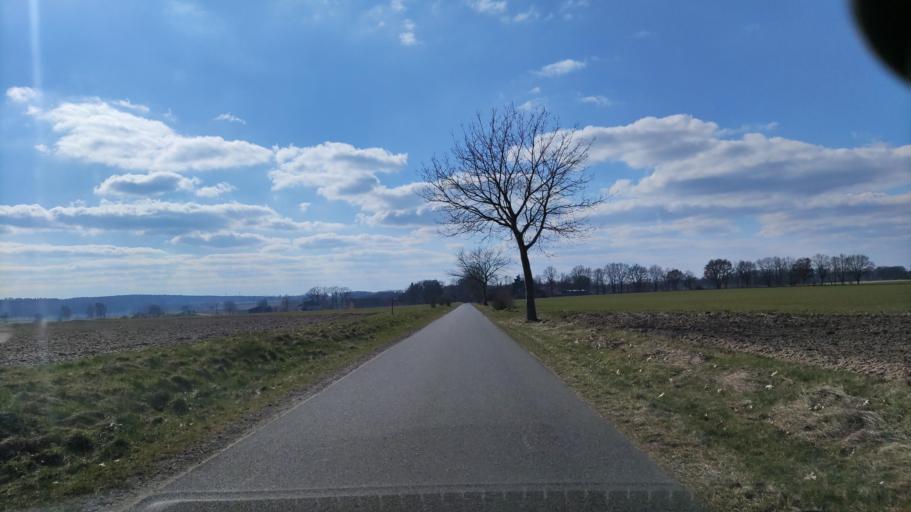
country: DE
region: Lower Saxony
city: Jelmstorf
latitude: 53.0958
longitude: 10.5118
